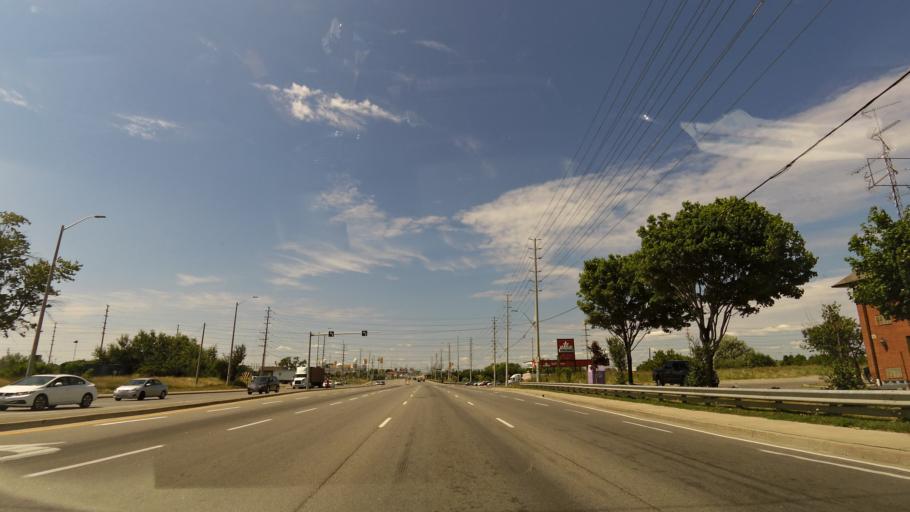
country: CA
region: Ontario
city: Brampton
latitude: 43.6743
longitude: -79.6730
